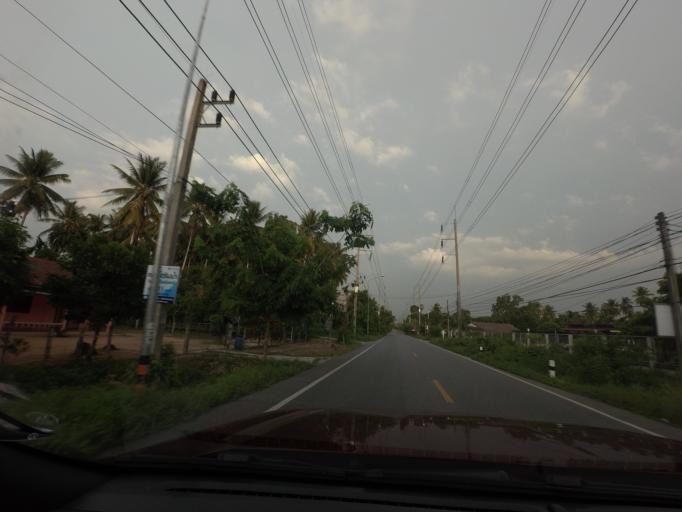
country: TH
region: Yala
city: Yala
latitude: 6.5732
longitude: 101.2013
